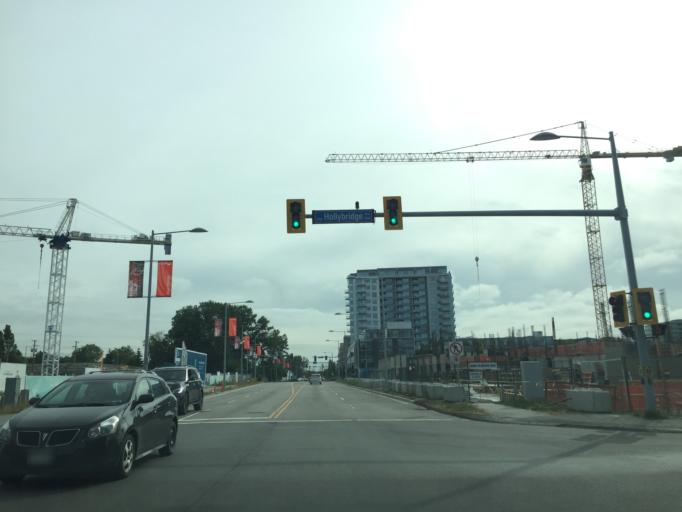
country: CA
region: British Columbia
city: Richmond
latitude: 49.1746
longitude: -123.1490
